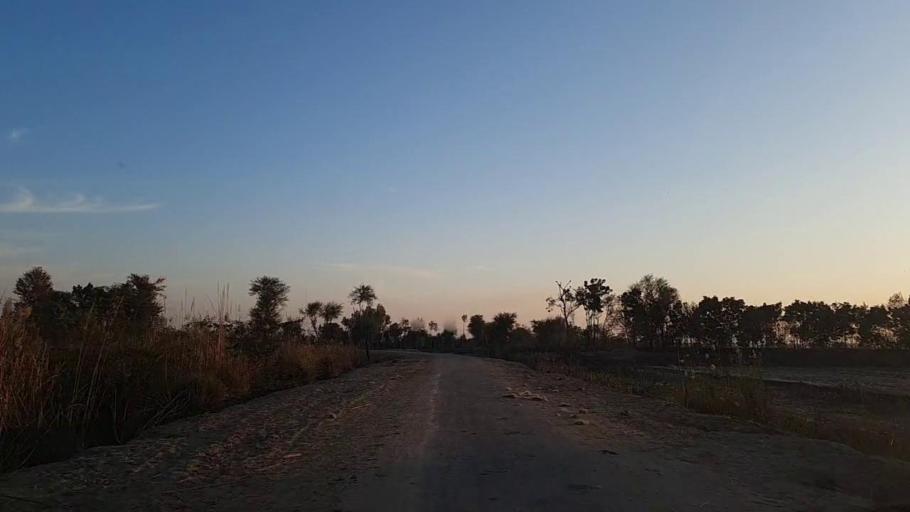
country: PK
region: Sindh
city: Bandhi
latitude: 26.6280
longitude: 68.3706
